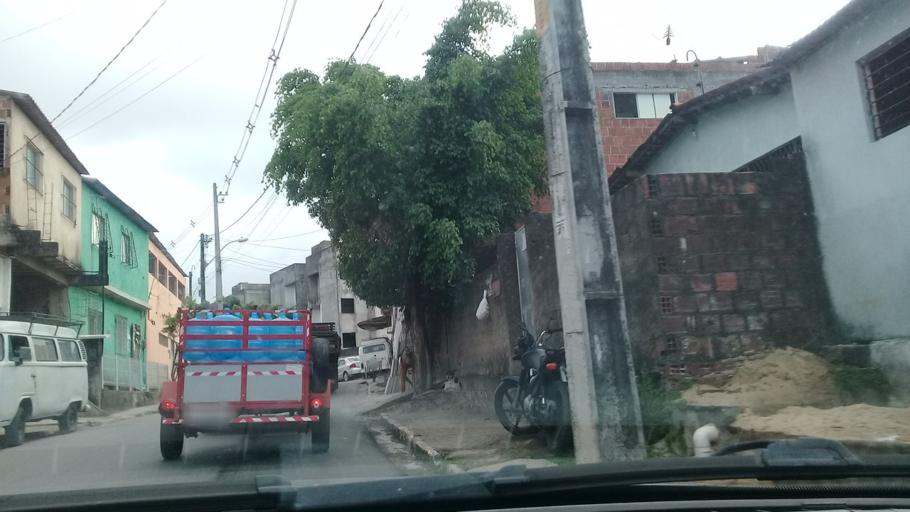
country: BR
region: Pernambuco
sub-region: Jaboatao Dos Guararapes
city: Jaboatao
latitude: -8.1378
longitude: -34.9444
